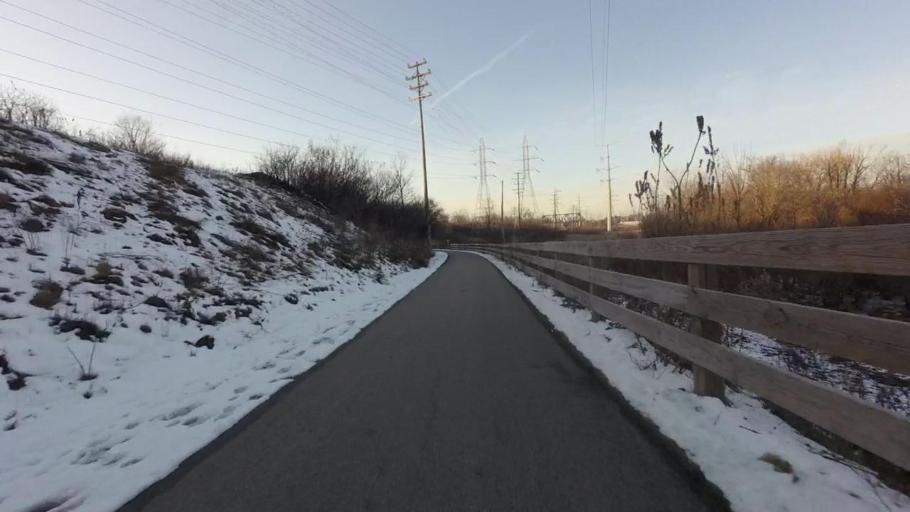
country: US
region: Wisconsin
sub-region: Milwaukee County
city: Glendale
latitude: 43.1282
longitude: -87.9451
